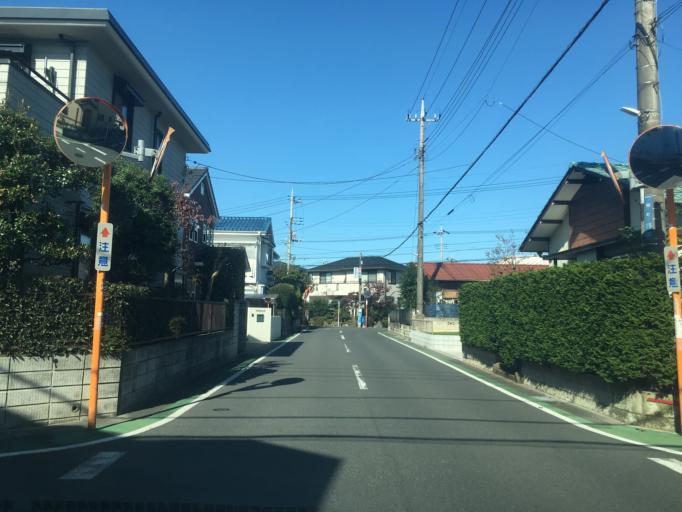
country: JP
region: Saitama
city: Sakado
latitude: 35.9629
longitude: 139.4081
